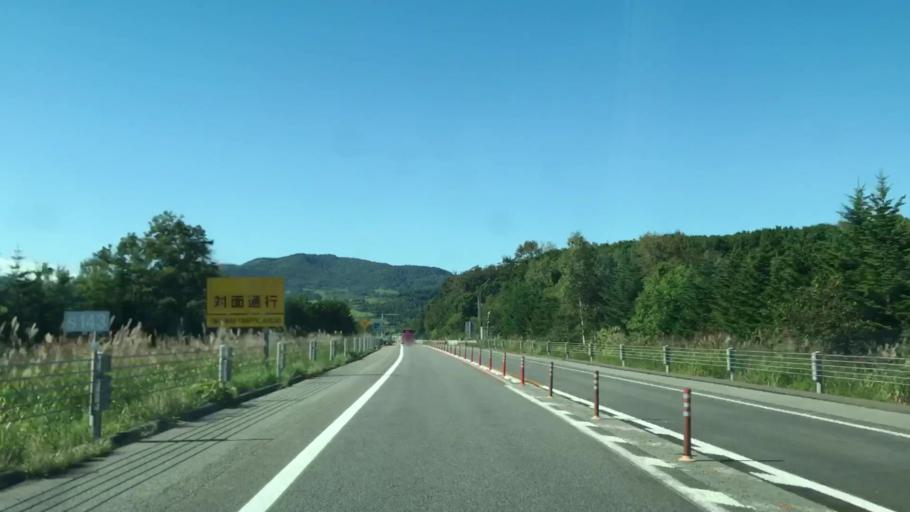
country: JP
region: Hokkaido
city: Date
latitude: 42.5340
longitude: 140.7985
